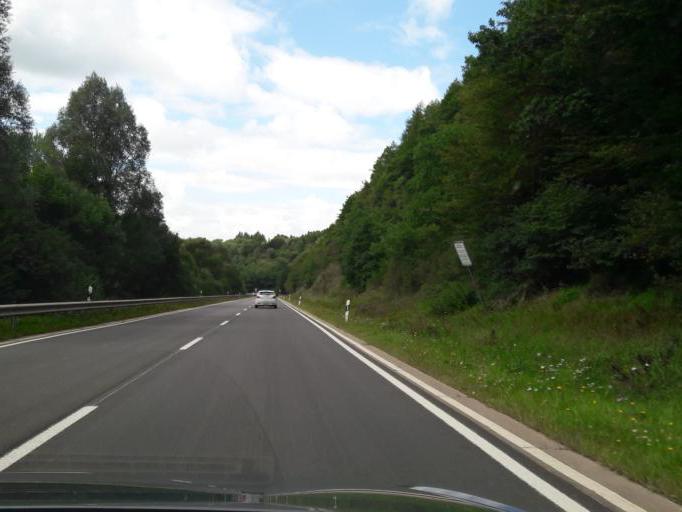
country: DE
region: Rheinland-Pfalz
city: Ruschberg
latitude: 49.6224
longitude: 7.2960
